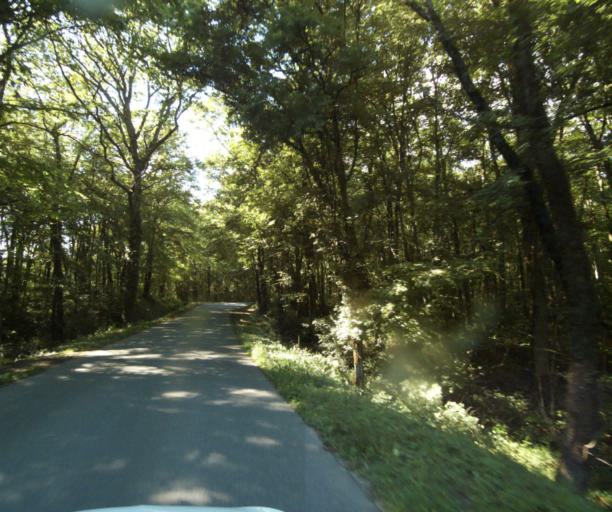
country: FR
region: Rhone-Alpes
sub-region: Departement de la Haute-Savoie
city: Massongy
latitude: 46.3339
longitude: 6.3279
